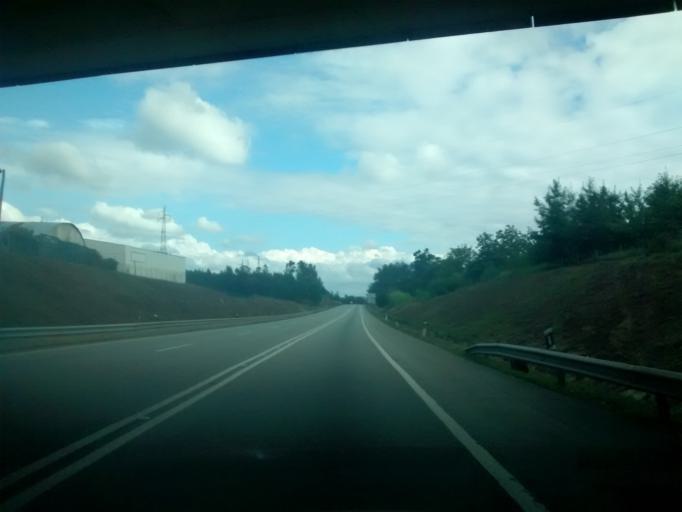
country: PT
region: Aveiro
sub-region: Agueda
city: Aguada de Cima
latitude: 40.5360
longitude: -8.4605
